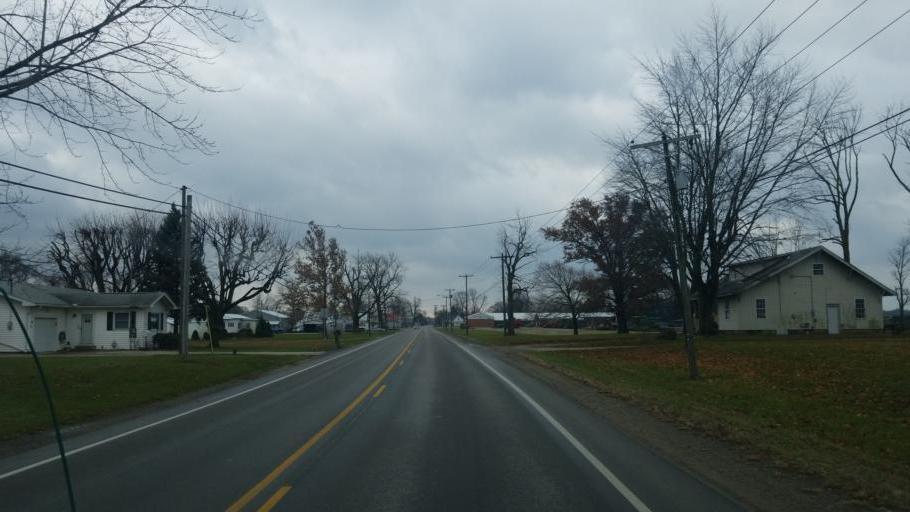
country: US
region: Indiana
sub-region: Adams County
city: Geneva
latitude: 40.5394
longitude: -84.9647
